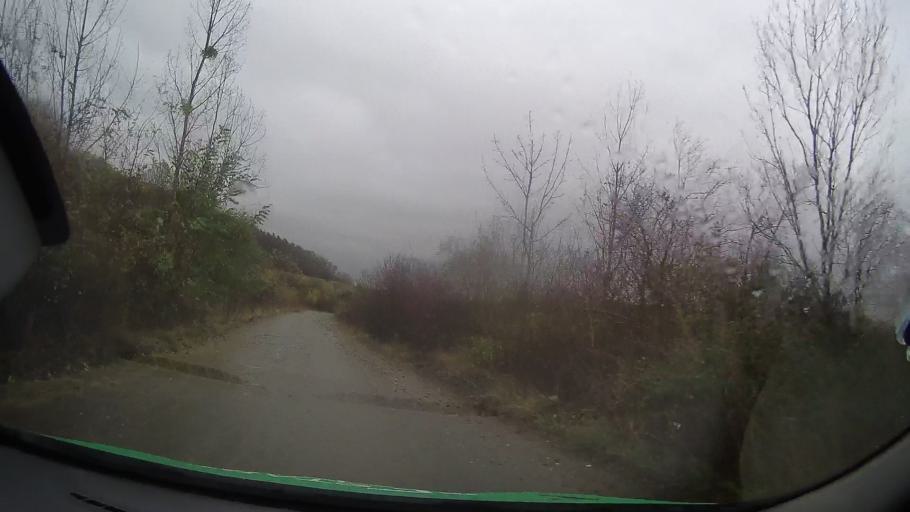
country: RO
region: Mures
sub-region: Comuna Vatava
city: Vatava
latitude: 46.9530
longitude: 24.7337
